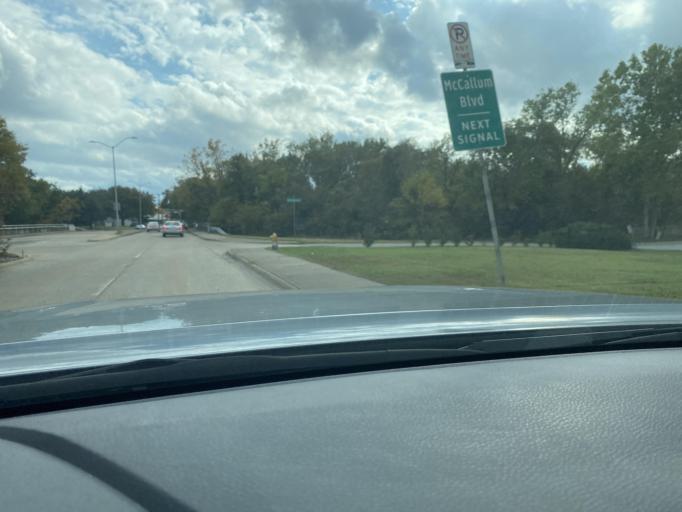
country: US
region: Texas
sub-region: Dallas County
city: Addison
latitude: 32.9897
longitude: -96.7844
